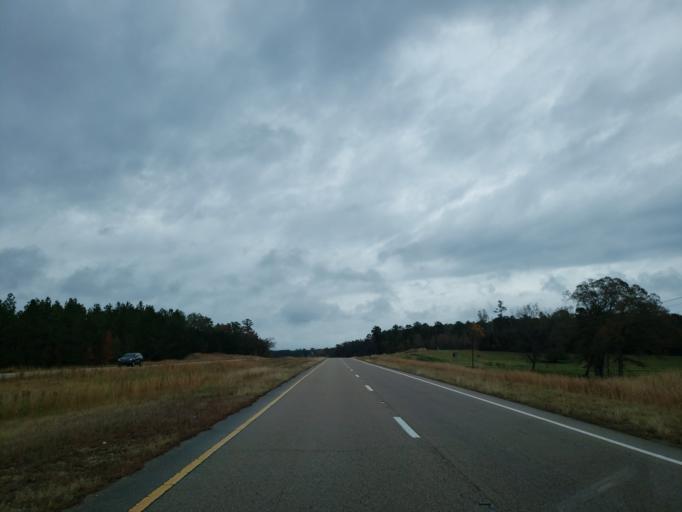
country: US
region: Mississippi
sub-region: Wayne County
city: Waynesboro
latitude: 31.7356
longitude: -88.6502
